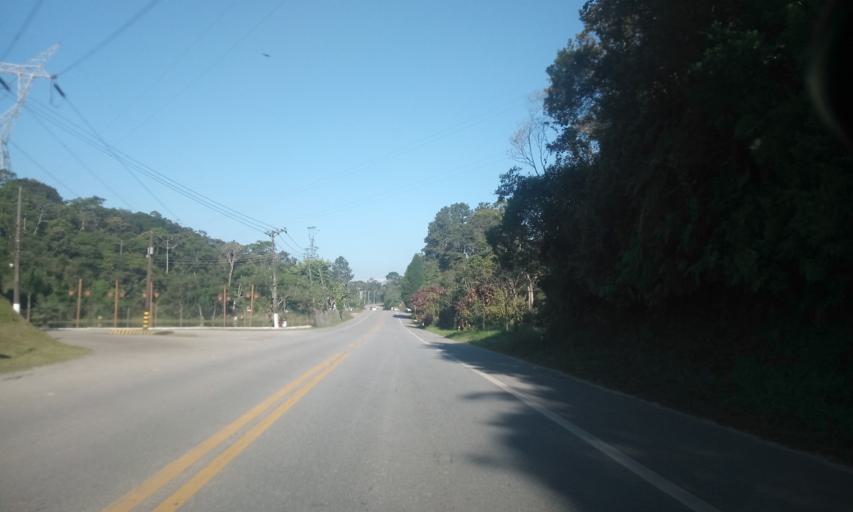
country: BR
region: Sao Paulo
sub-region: Cubatao
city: Cubatao
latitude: -23.8101
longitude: -46.4874
